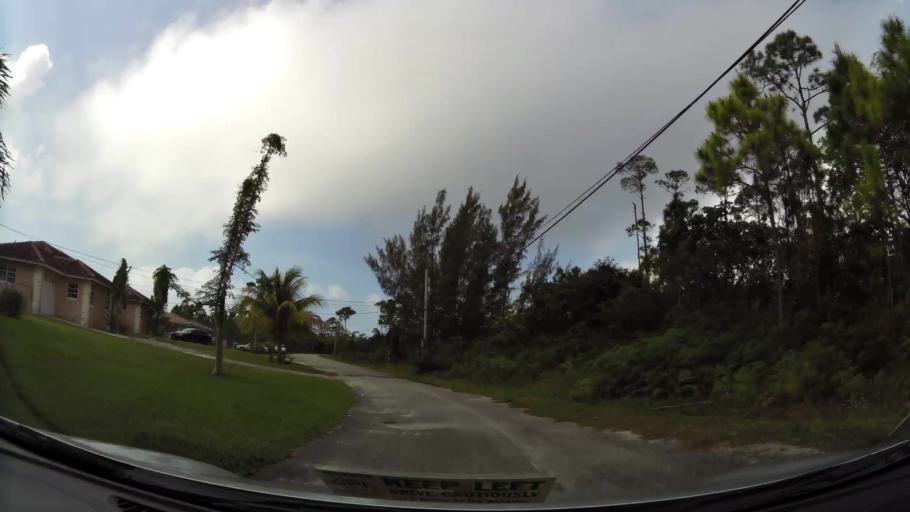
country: BS
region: Freeport
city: Lucaya
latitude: 26.5409
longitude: -78.5935
